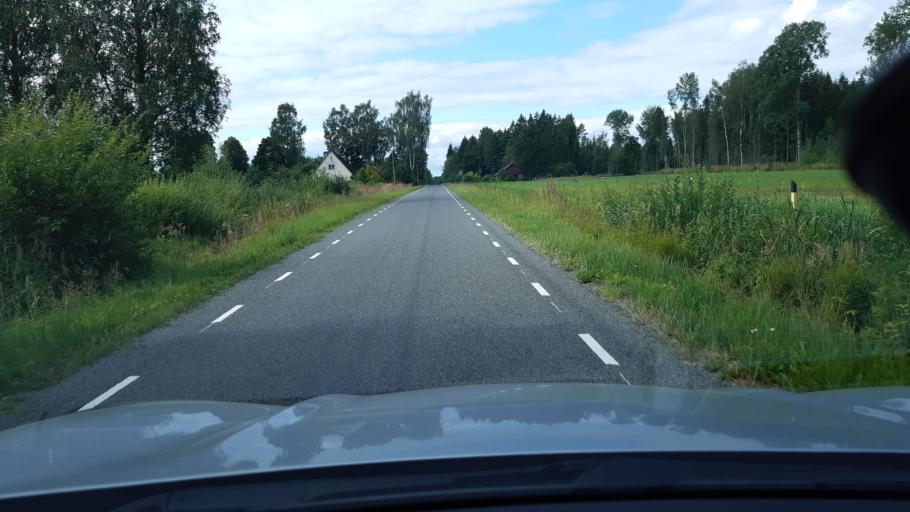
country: EE
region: Raplamaa
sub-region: Jaervakandi vald
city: Jarvakandi
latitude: 58.7514
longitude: 24.9236
